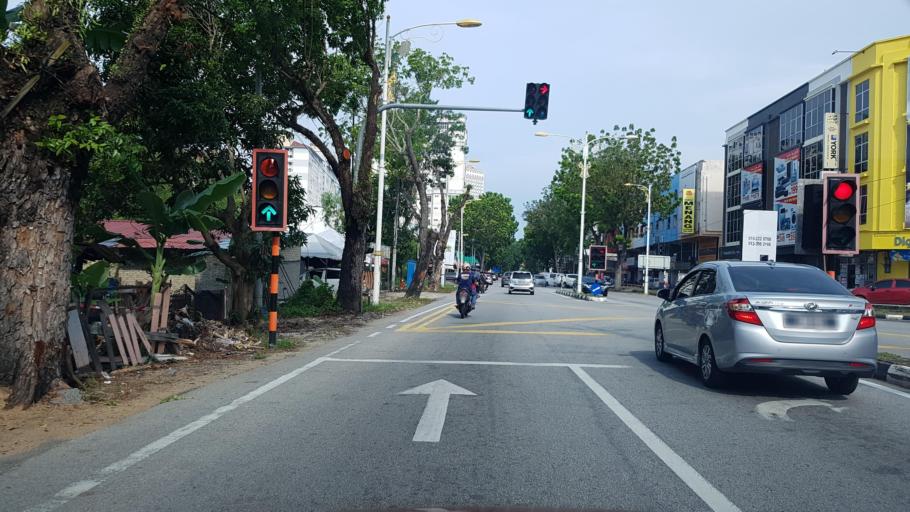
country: MY
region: Terengganu
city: Kuala Terengganu
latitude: 5.3321
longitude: 103.1432
